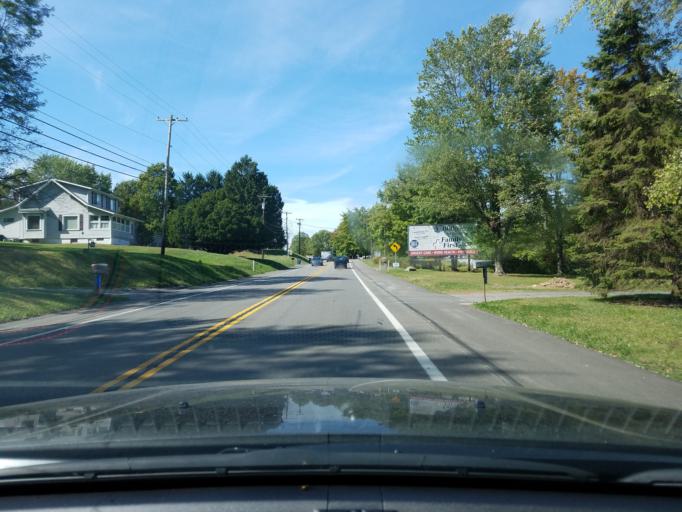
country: US
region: Pennsylvania
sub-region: Lawrence County
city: New Castle
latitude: 40.9586
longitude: -80.2890
